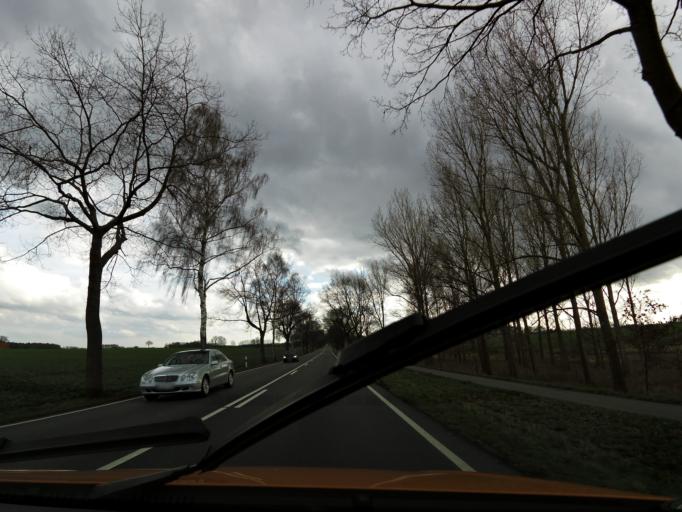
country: DE
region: Lower Saxony
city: Bassum
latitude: 52.8816
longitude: 8.7288
